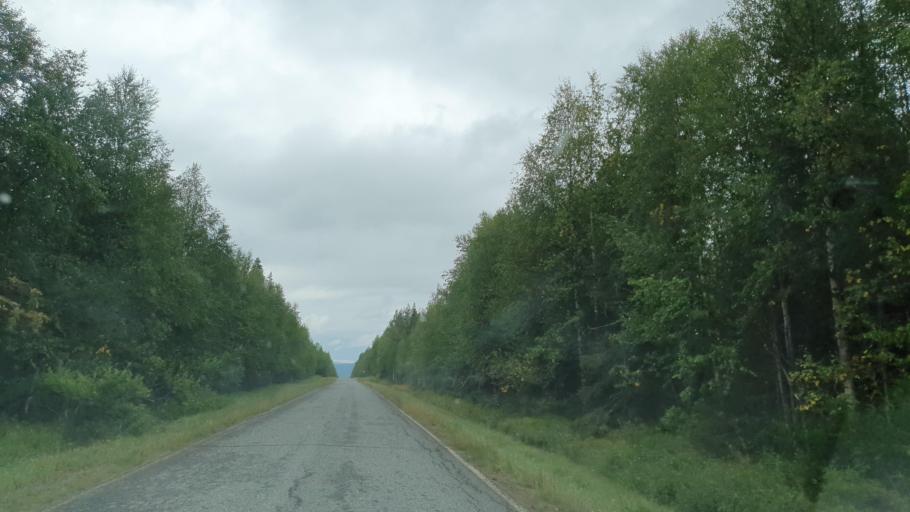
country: FI
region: Lapland
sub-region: Tunturi-Lappi
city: Kittilae
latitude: 67.7346
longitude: 24.3924
